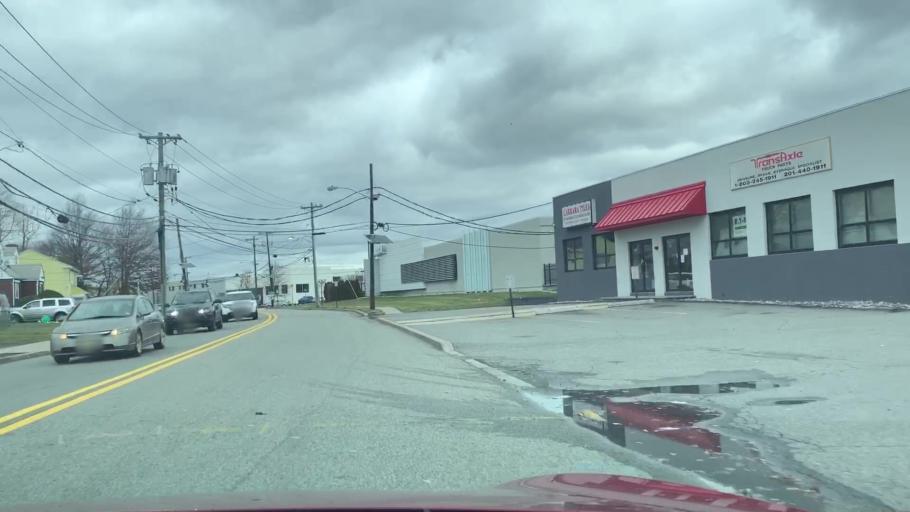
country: US
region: New Jersey
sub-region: Bergen County
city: Little Ferry
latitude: 40.8614
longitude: -74.0492
